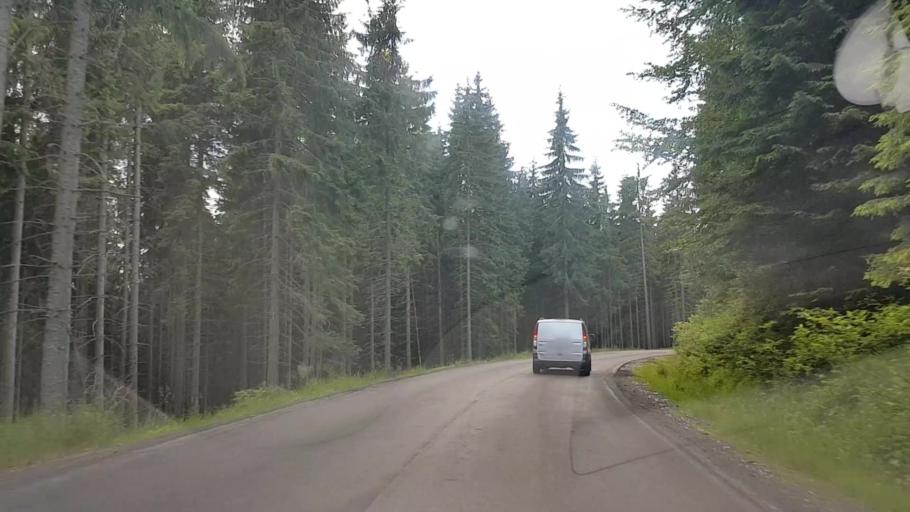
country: RO
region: Harghita
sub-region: Comuna Varsag
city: Varsag
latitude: 46.6602
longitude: 25.3015
